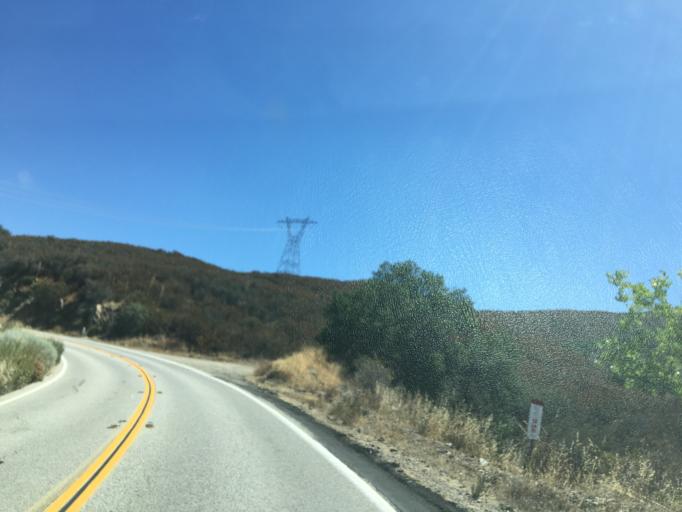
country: US
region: California
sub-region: Los Angeles County
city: Green Valley
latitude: 34.5717
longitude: -118.3880
